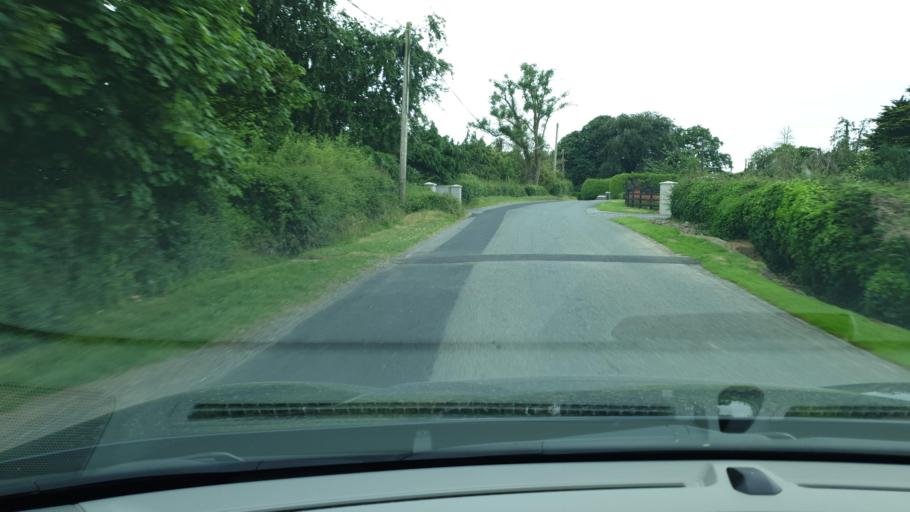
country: IE
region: Leinster
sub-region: An Mhi
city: Ashbourne
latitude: 53.4635
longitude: -6.3803
